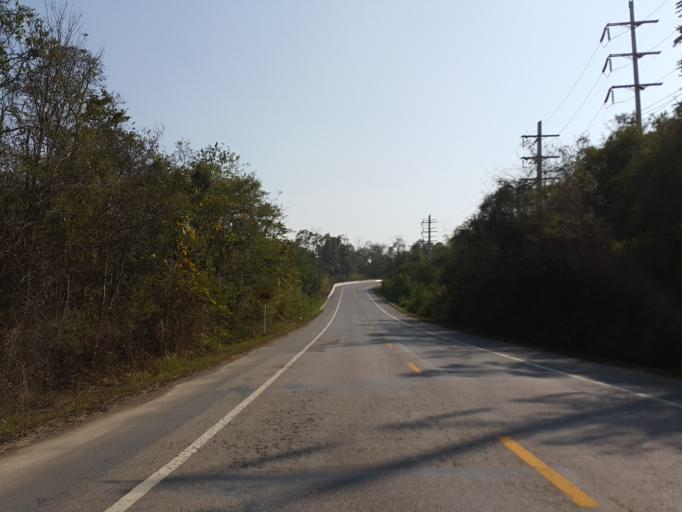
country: TH
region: Lampang
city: Chae Hom
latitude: 18.6041
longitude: 99.5477
